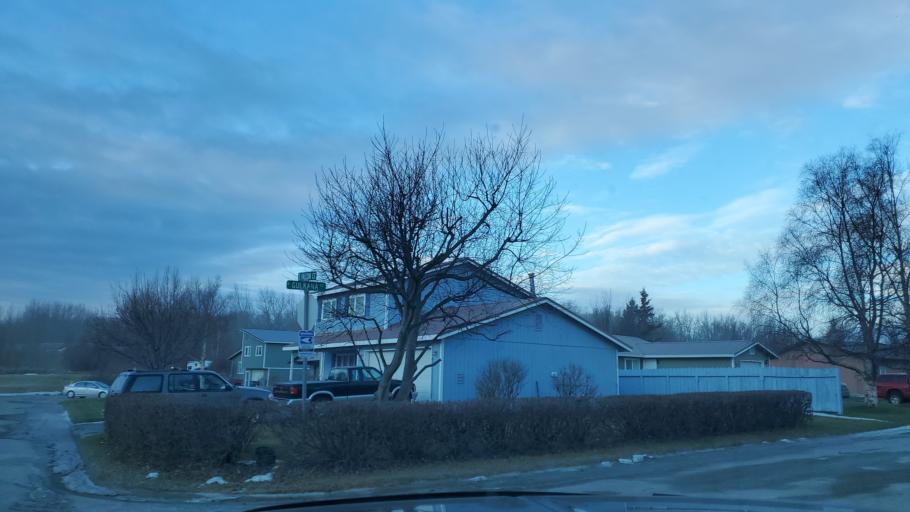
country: US
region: Alaska
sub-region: Matanuska-Susitna Borough
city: Palmer
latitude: 61.6147
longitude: -149.1040
